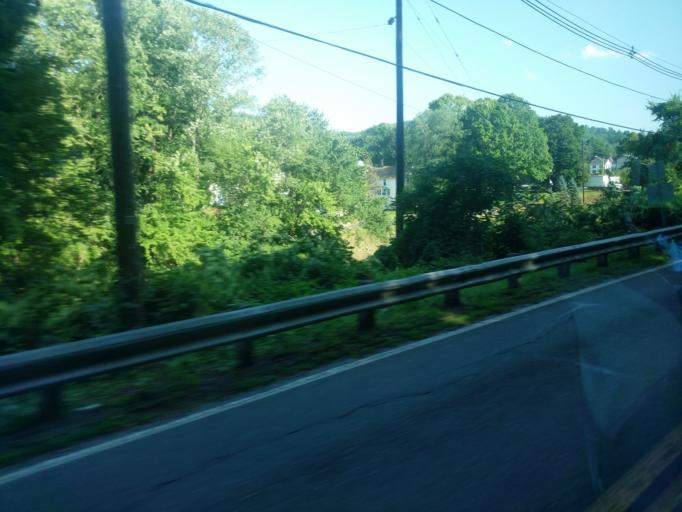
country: US
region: Massachusetts
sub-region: Berkshire County
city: Great Barrington
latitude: 42.2028
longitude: -73.3583
